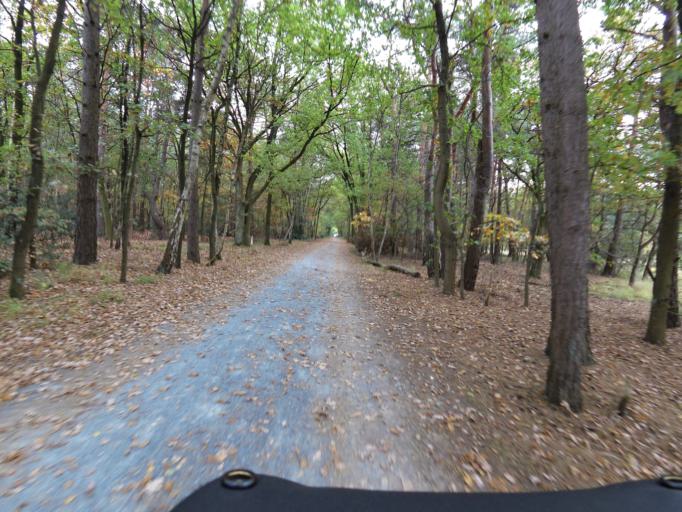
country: BE
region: Flanders
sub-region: Provincie Antwerpen
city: Kalmthout
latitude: 51.3717
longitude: 4.4553
